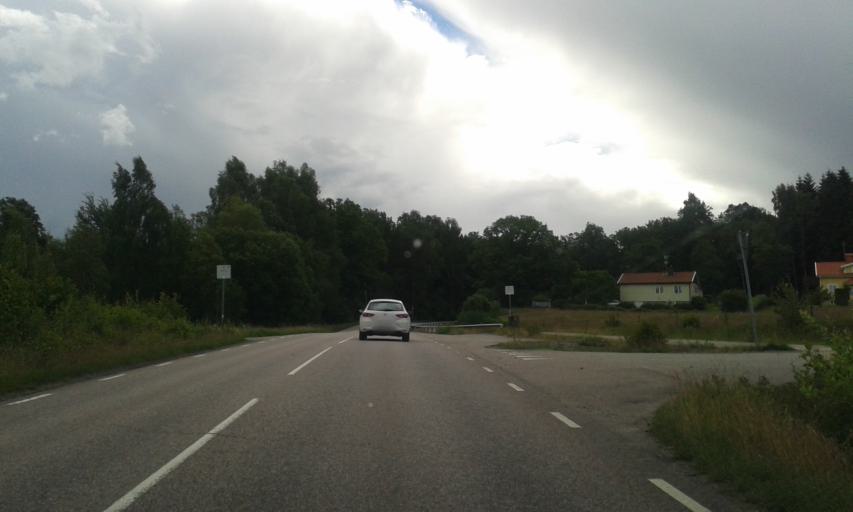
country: SE
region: Vaestra Goetaland
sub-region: Kungalvs Kommun
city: Diserod
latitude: 57.9039
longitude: 12.0084
